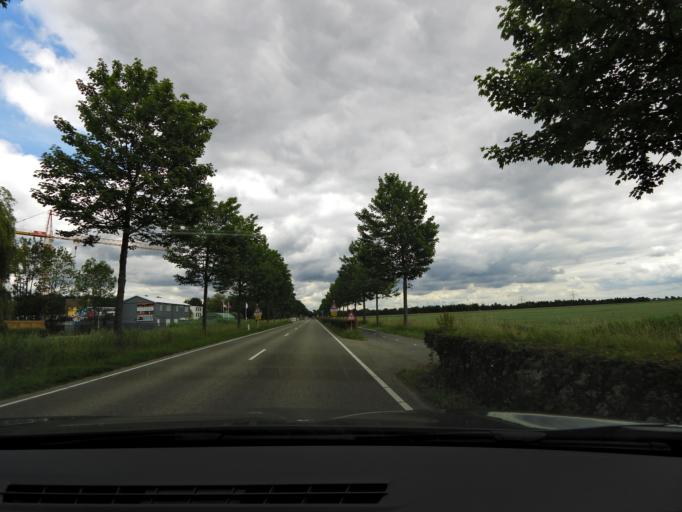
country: NL
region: South Holland
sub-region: Gemeente Oud-Beijerland
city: Oud-Beijerland
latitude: 51.8149
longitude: 4.4023
